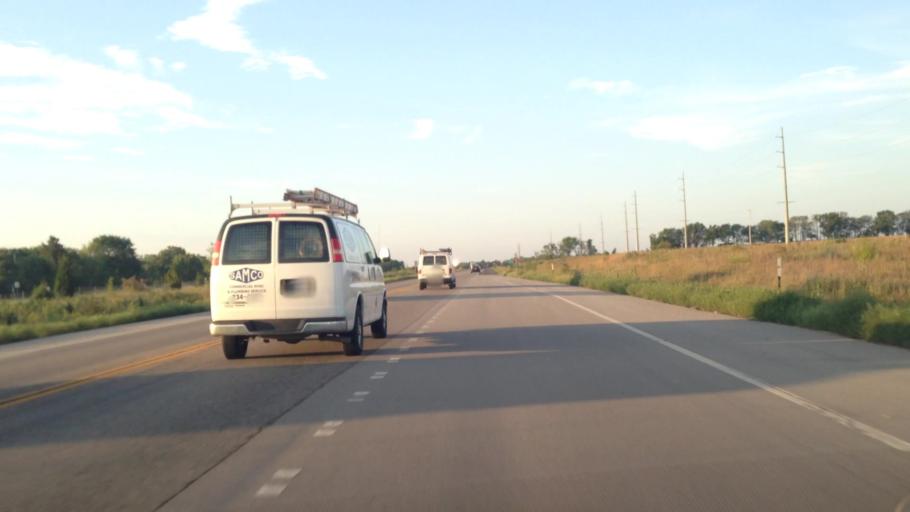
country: US
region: Kansas
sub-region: Douglas County
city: Lawrence
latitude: 38.9531
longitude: -95.3352
